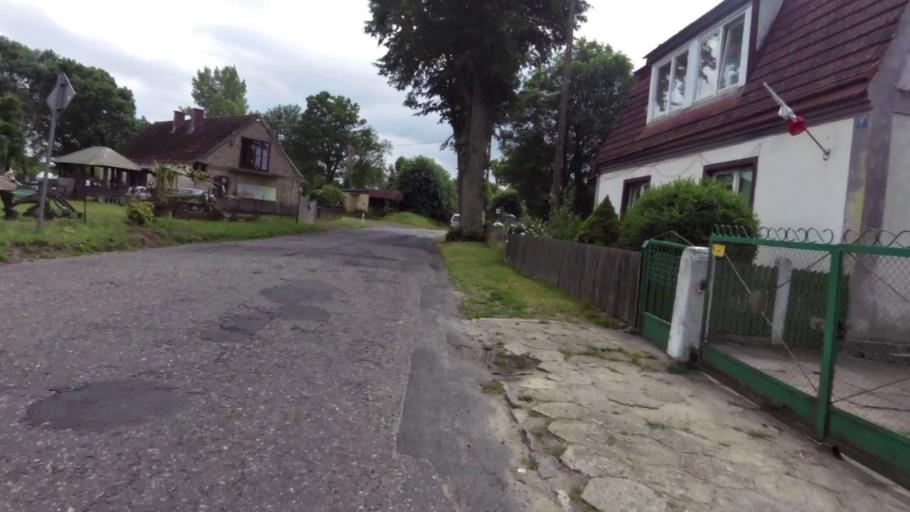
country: PL
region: West Pomeranian Voivodeship
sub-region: Powiat goleniowski
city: Stepnica
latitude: 53.6985
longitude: 14.5475
